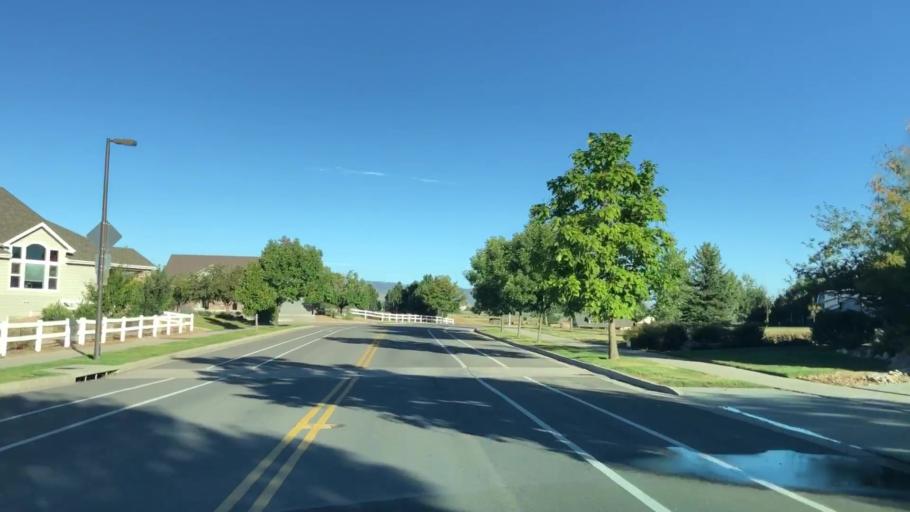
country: US
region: Colorado
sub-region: Larimer County
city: Loveland
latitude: 40.4617
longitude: -105.0355
